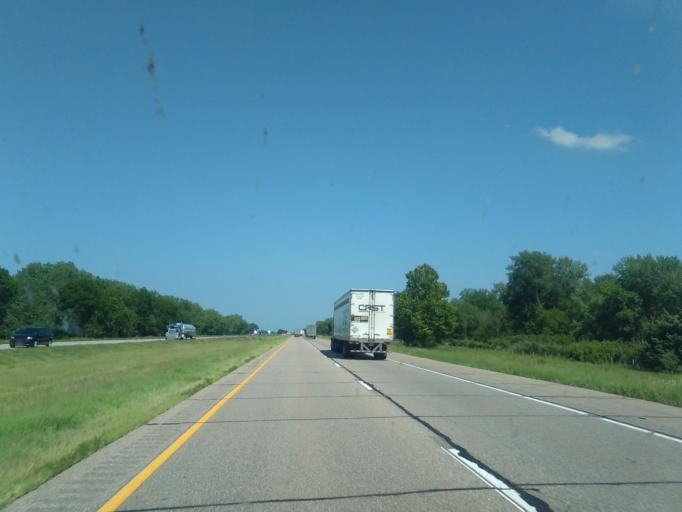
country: US
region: Nebraska
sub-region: Buffalo County
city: Kearney
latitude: 40.6724
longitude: -99.2007
